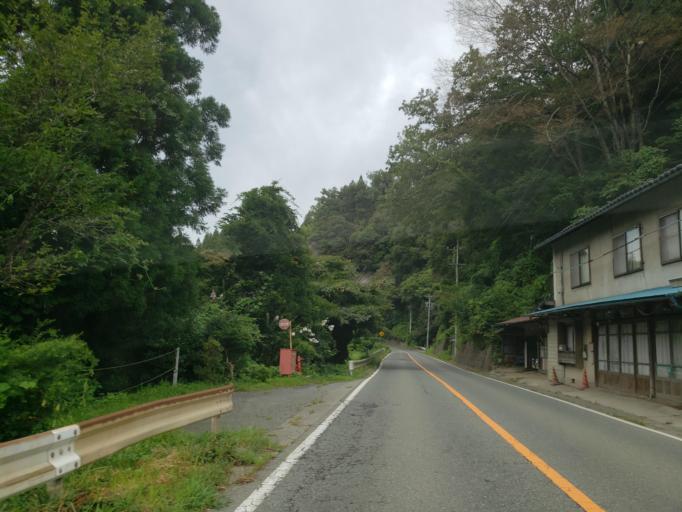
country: JP
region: Nagano
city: Nagano-shi
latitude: 36.6130
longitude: 138.0497
